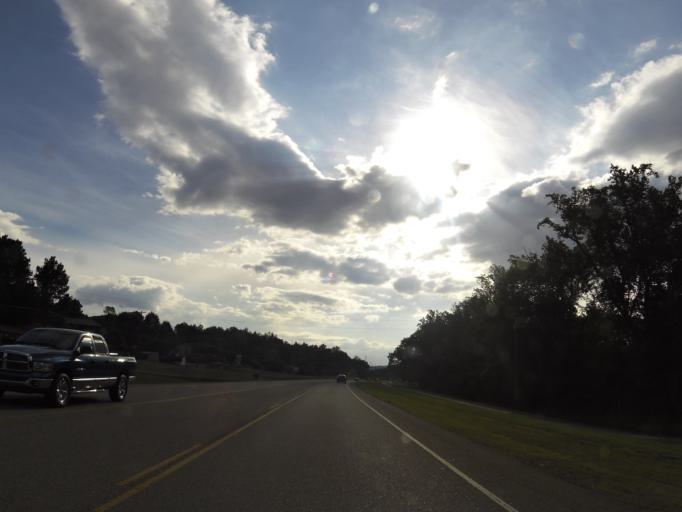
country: US
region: Tennessee
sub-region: Blount County
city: Wildwood
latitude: 35.6784
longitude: -83.7283
